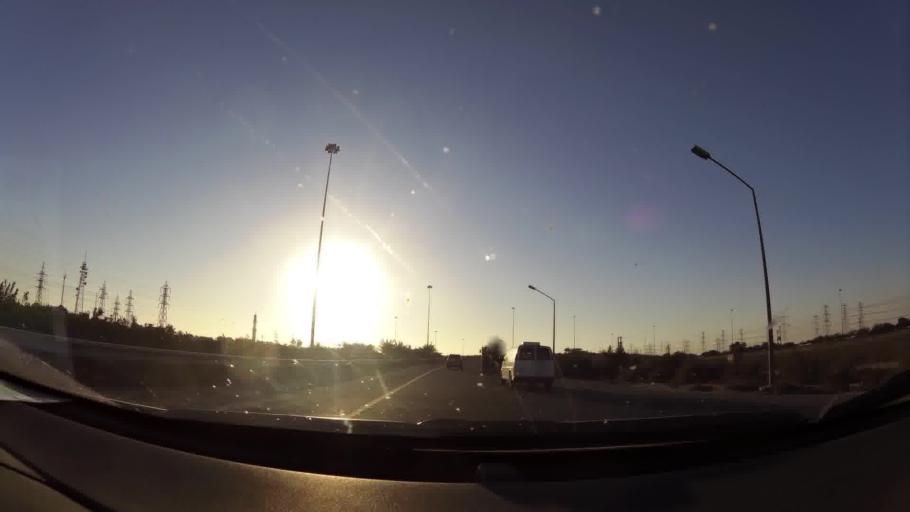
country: KW
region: Al Ahmadi
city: Al Fahahil
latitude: 28.9242
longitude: 48.2030
